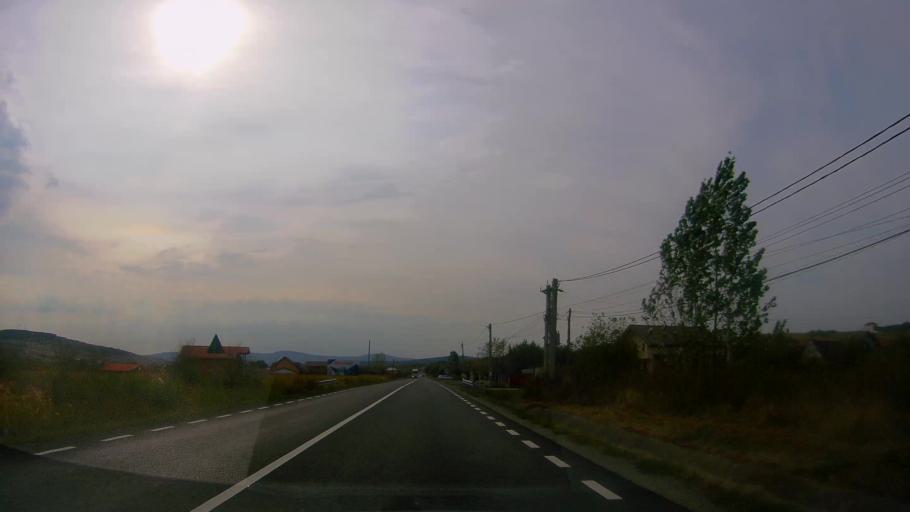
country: RO
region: Salaj
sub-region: Comuna Hereclean
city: Hereclean
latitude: 47.2504
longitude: 22.9836
